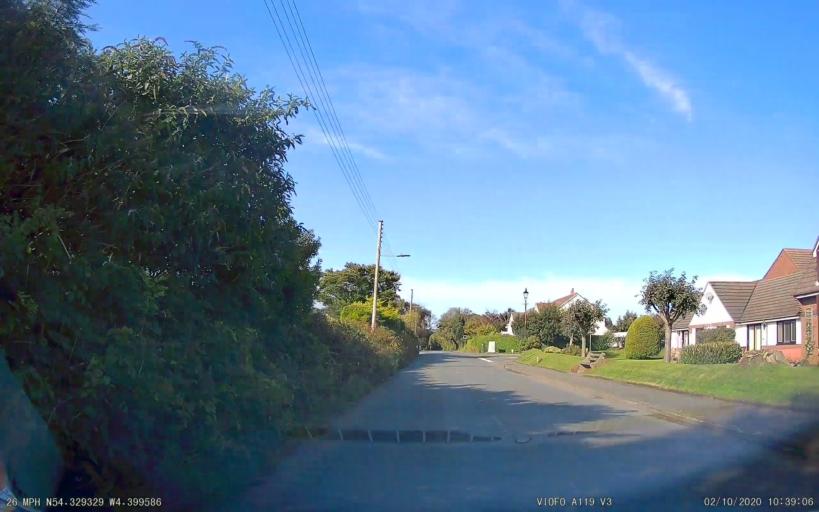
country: IM
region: Ramsey
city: Ramsey
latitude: 54.3293
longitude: -4.3996
